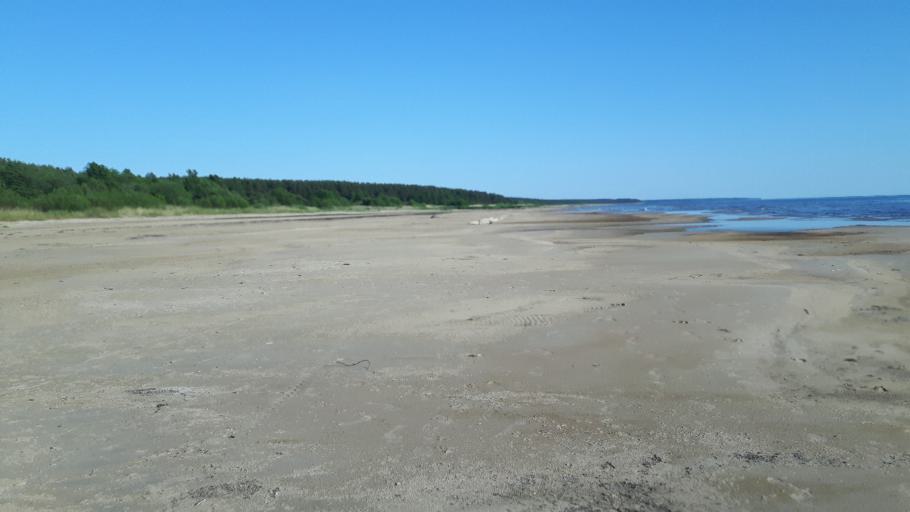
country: LV
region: Salacgrivas
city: Salacgriva
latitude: 57.6888
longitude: 24.3554
